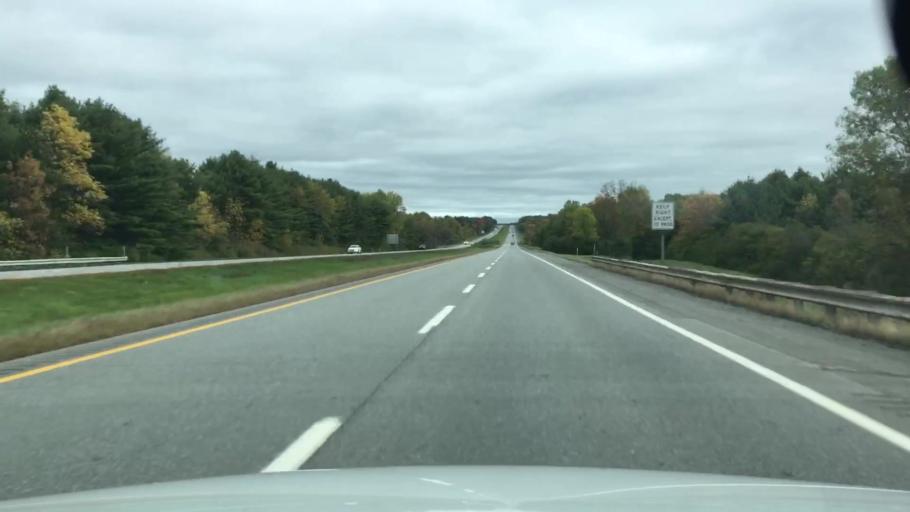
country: US
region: Maine
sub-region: Penobscot County
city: Newport
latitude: 44.8280
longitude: -69.2796
